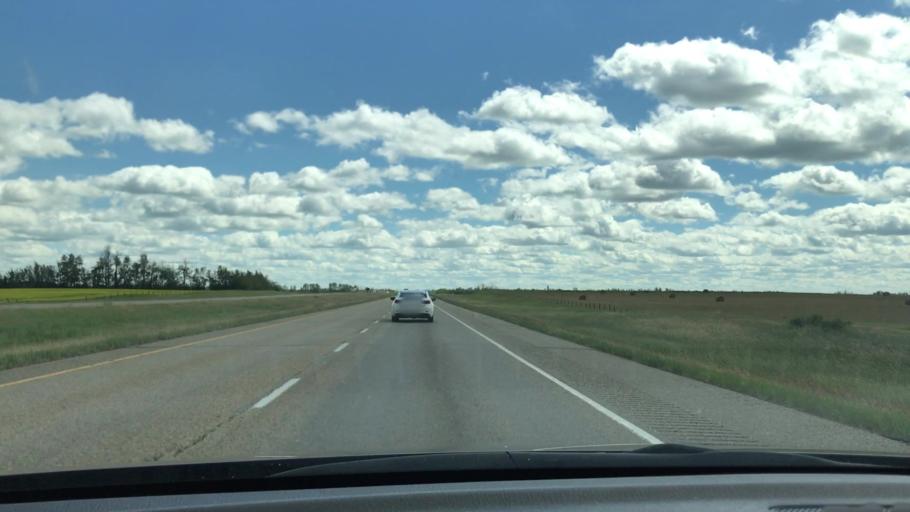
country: CA
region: Alberta
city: Leduc
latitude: 53.1593
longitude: -113.5985
